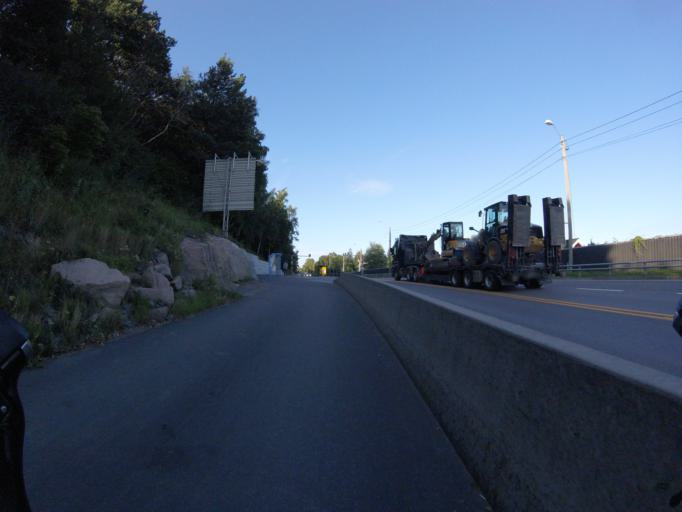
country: NO
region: Akershus
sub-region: Lorenskog
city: Kjenn
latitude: 59.9602
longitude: 10.8947
